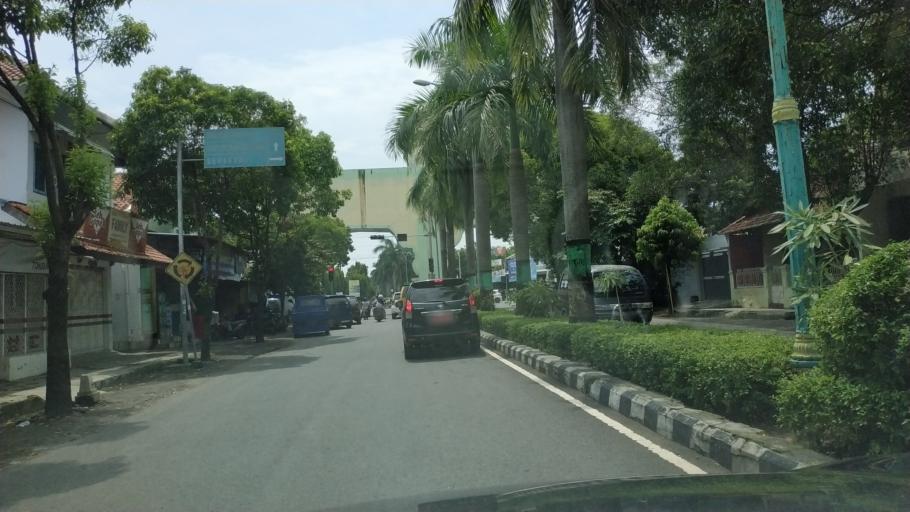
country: ID
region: Central Java
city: Slawi
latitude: -6.9806
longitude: 109.1271
